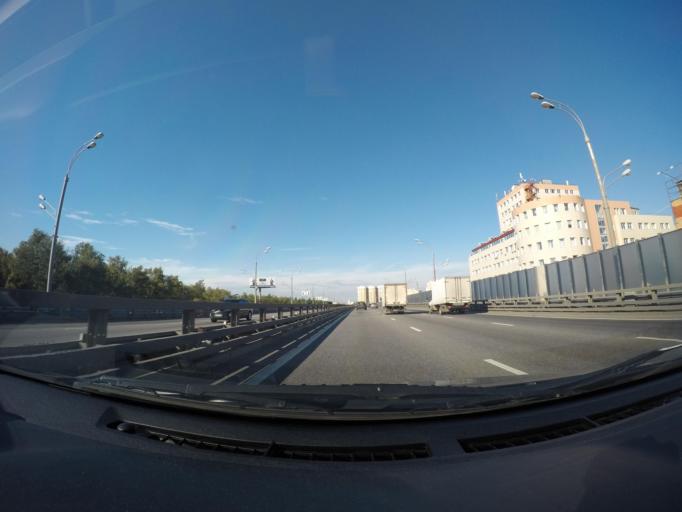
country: RU
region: Moscow
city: Zhulebino
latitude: 55.6774
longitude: 37.8536
